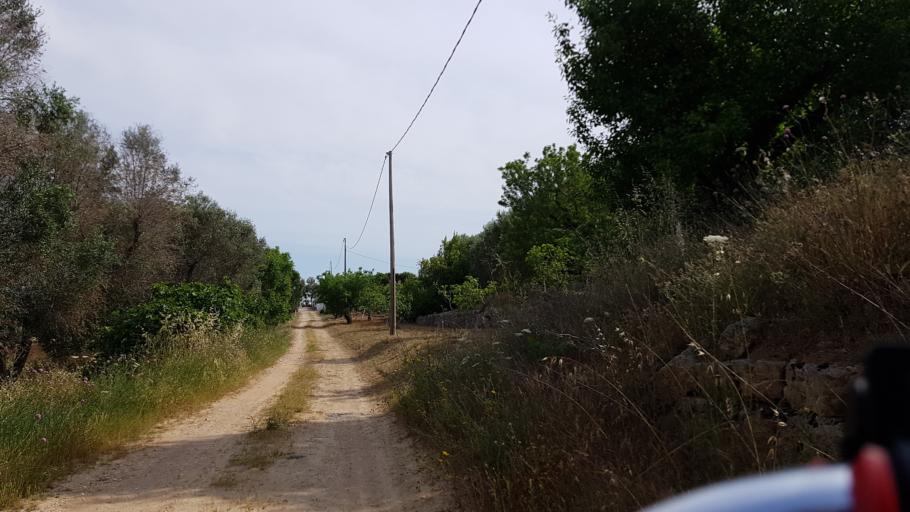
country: IT
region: Apulia
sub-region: Provincia di Brindisi
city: San Vito dei Normanni
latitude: 40.6553
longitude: 17.8000
